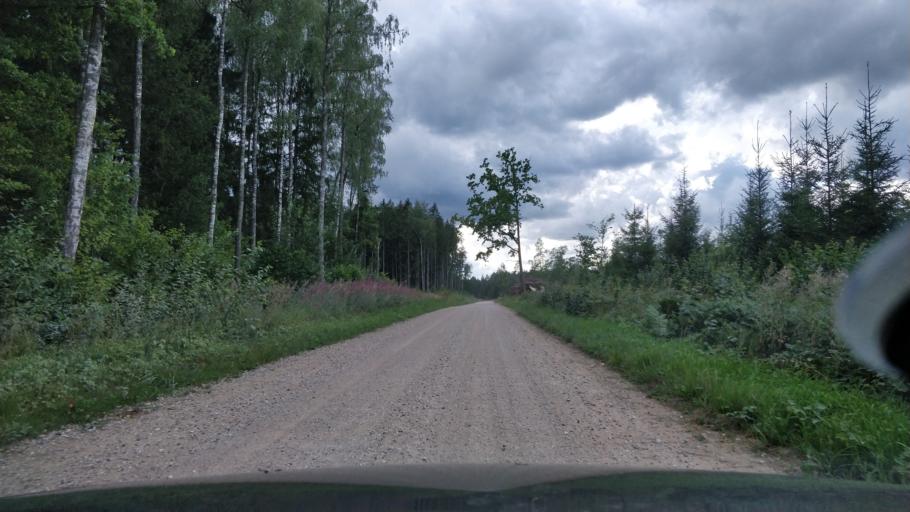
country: LV
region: Kegums
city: Kegums
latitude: 56.8060
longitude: 24.6969
